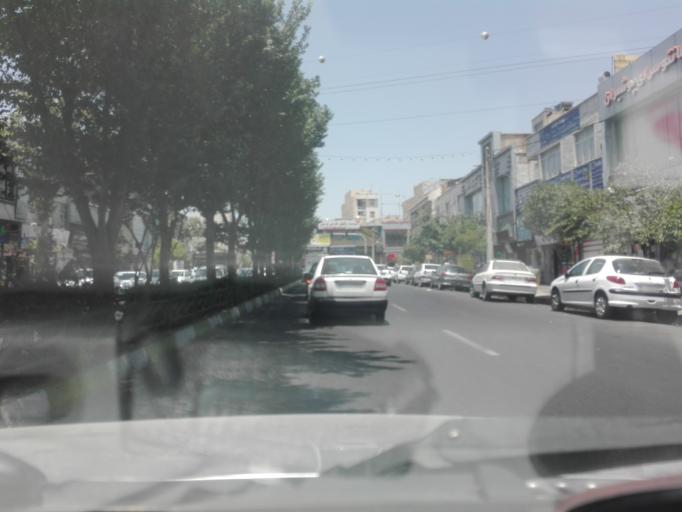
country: IR
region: Tehran
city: Shahre Jadide Andisheh
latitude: 35.7361
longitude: 50.9915
